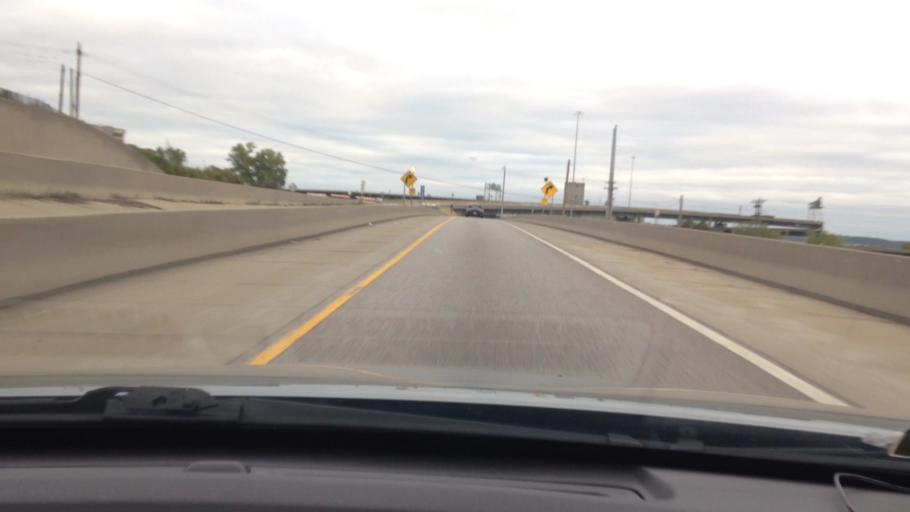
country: US
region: Kansas
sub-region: Wyandotte County
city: Kansas City
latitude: 39.1114
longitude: -94.6187
